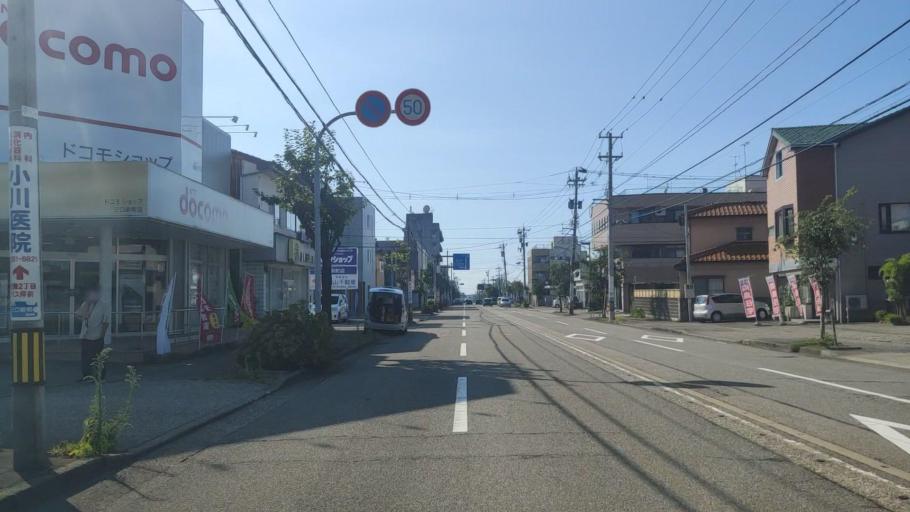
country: JP
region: Ishikawa
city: Nonoichi
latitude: 36.5444
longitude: 136.6777
